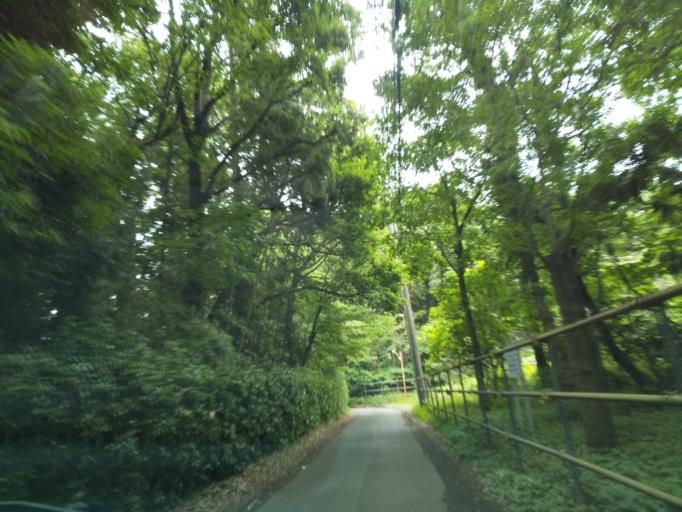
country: JP
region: Kanagawa
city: Zama
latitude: 35.5441
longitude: 139.3787
